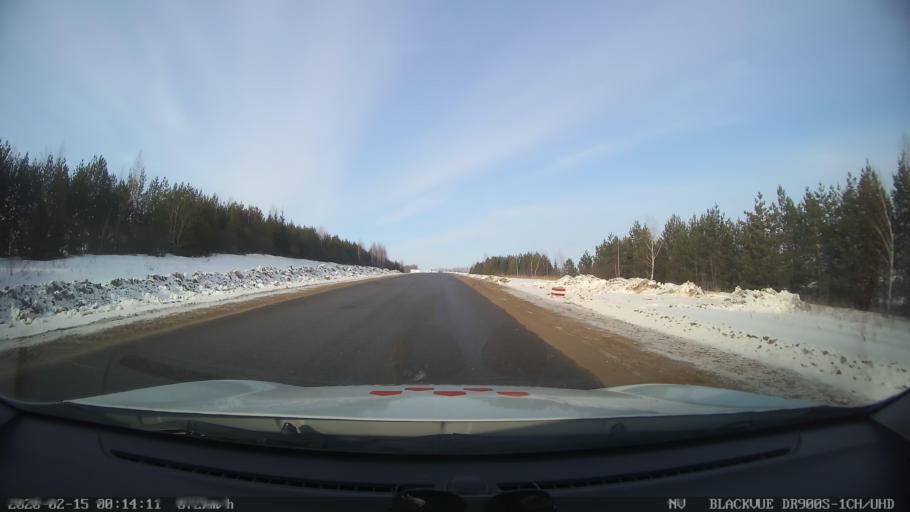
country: RU
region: Tatarstan
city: Stolbishchi
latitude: 55.4834
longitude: 49.0044
